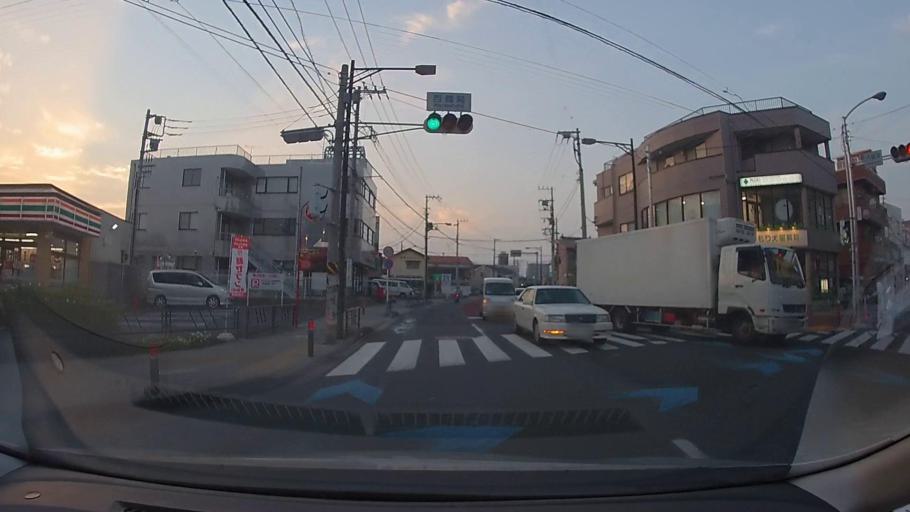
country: JP
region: Kanagawa
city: Minami-rinkan
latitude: 35.4877
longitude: 139.4485
